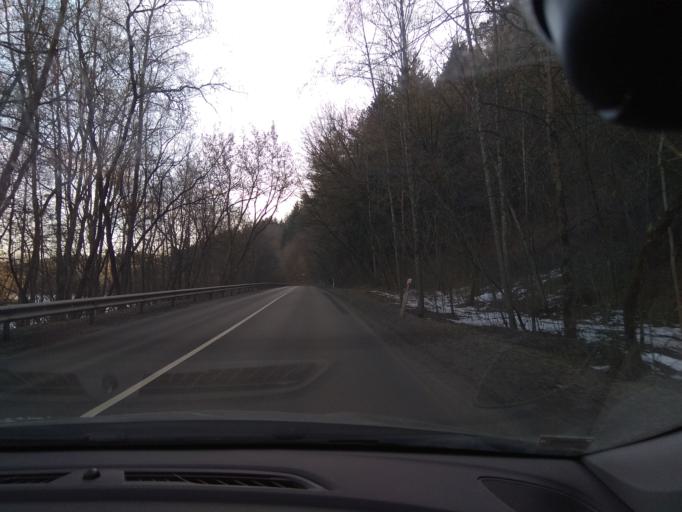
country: LT
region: Vilnius County
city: Lazdynai
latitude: 54.6596
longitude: 25.1748
